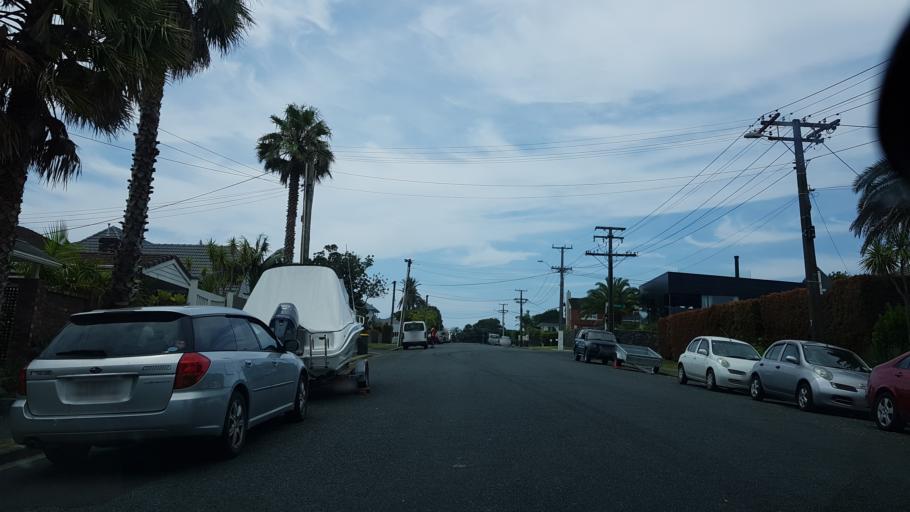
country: NZ
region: Auckland
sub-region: Auckland
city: North Shore
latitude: -36.7998
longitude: 174.7826
